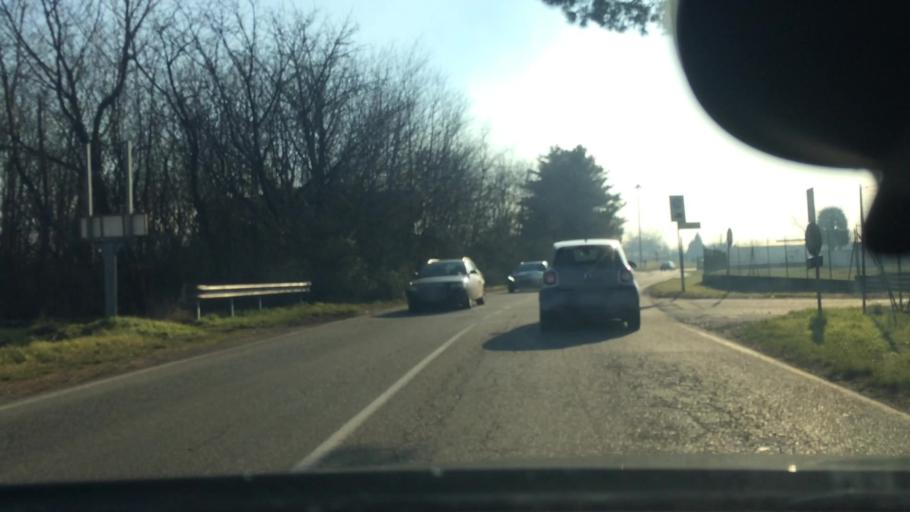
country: IT
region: Lombardy
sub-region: Citta metropolitana di Milano
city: Arluno
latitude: 45.5070
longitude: 8.9300
